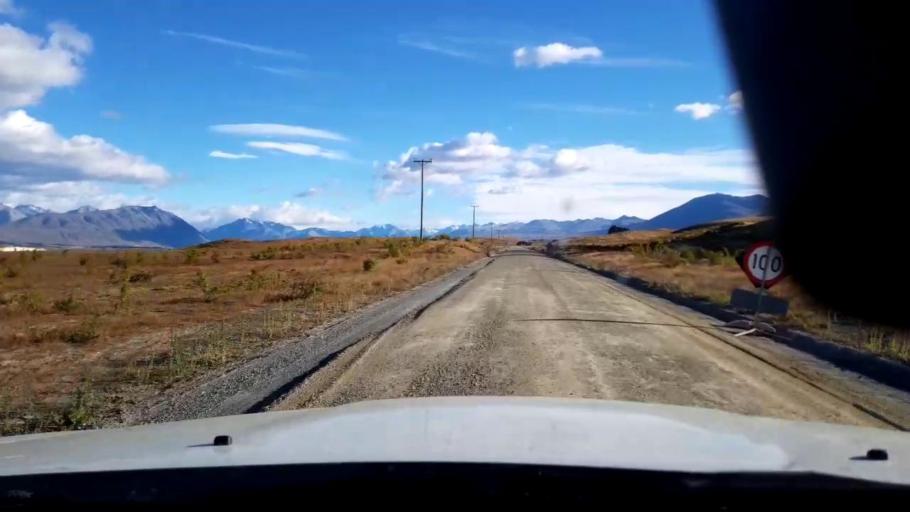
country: NZ
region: Canterbury
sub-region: Timaru District
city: Pleasant Point
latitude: -43.9814
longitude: 170.5087
